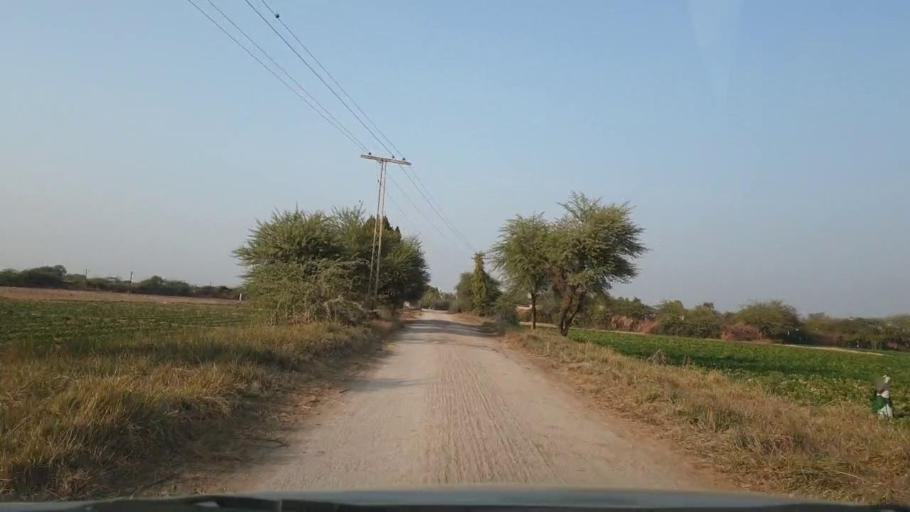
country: PK
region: Sindh
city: Tando Adam
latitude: 25.6873
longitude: 68.6327
